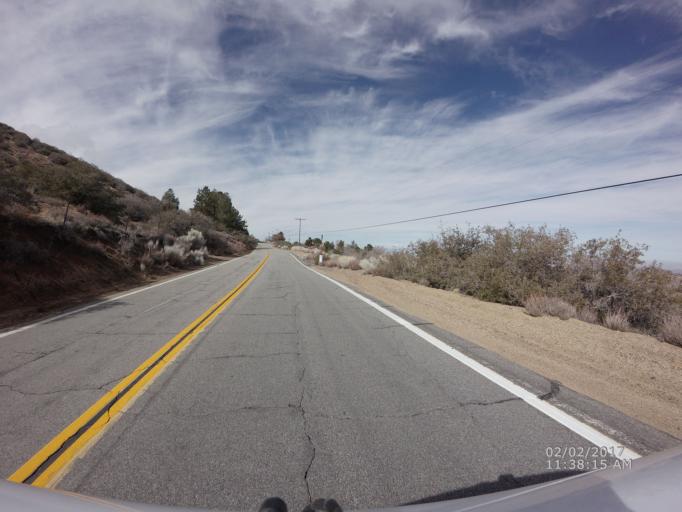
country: US
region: California
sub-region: Los Angeles County
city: Littlerock
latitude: 34.4297
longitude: -117.9202
